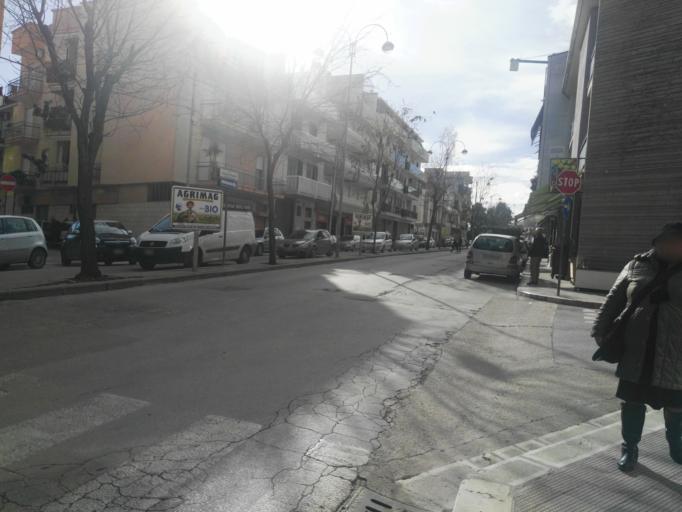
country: IT
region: Apulia
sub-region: Provincia di Barletta - Andria - Trani
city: Andria
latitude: 41.2214
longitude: 16.3063
